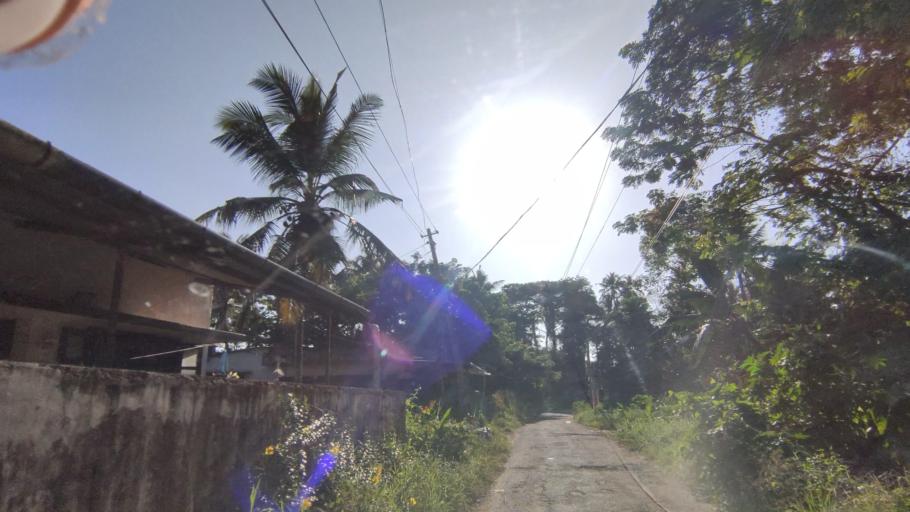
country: IN
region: Kerala
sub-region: Kottayam
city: Kottayam
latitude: 9.5924
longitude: 76.5075
